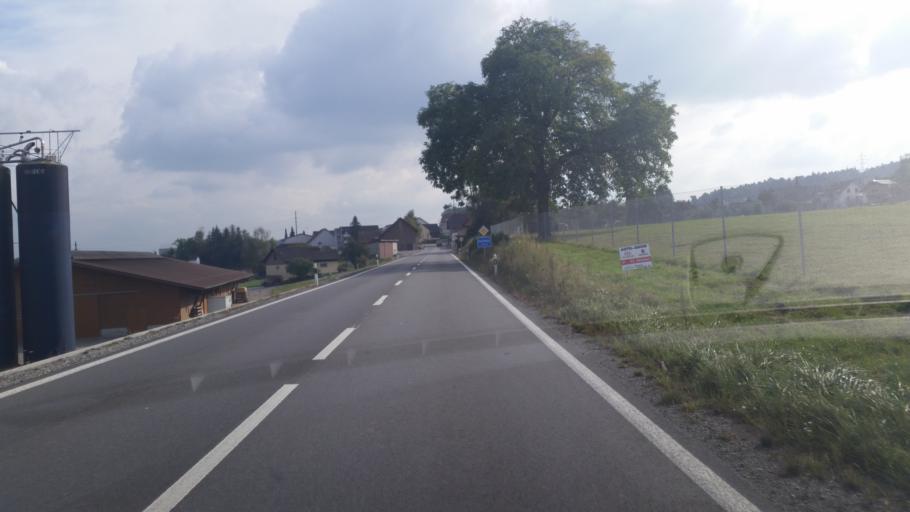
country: CH
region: Aargau
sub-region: Bezirk Baden
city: Mellingen
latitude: 47.3925
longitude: 8.2928
